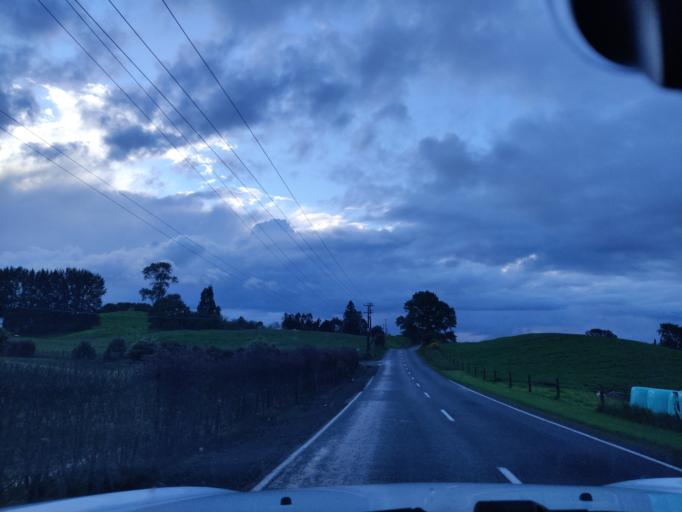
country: NZ
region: Waikato
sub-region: South Waikato District
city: Tokoroa
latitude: -38.2140
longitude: 175.8278
